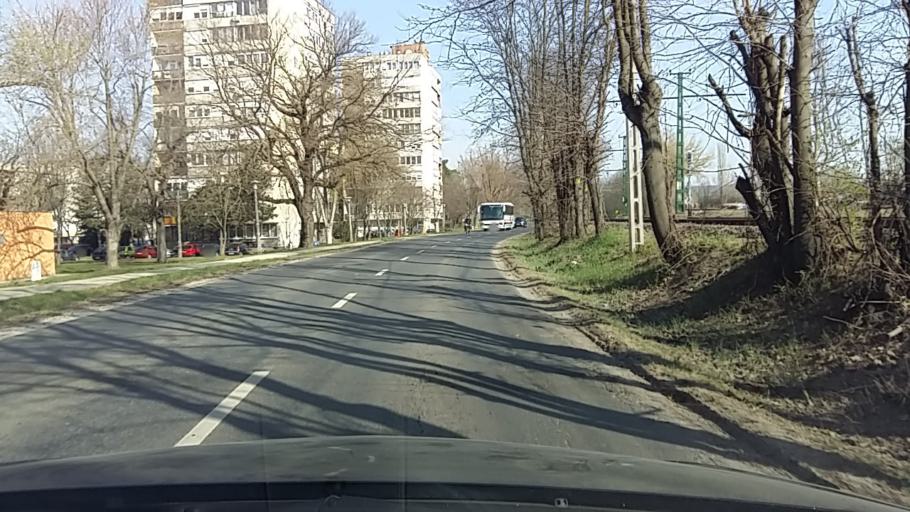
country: HU
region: Pest
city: Godollo
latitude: 47.5957
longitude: 19.3569
